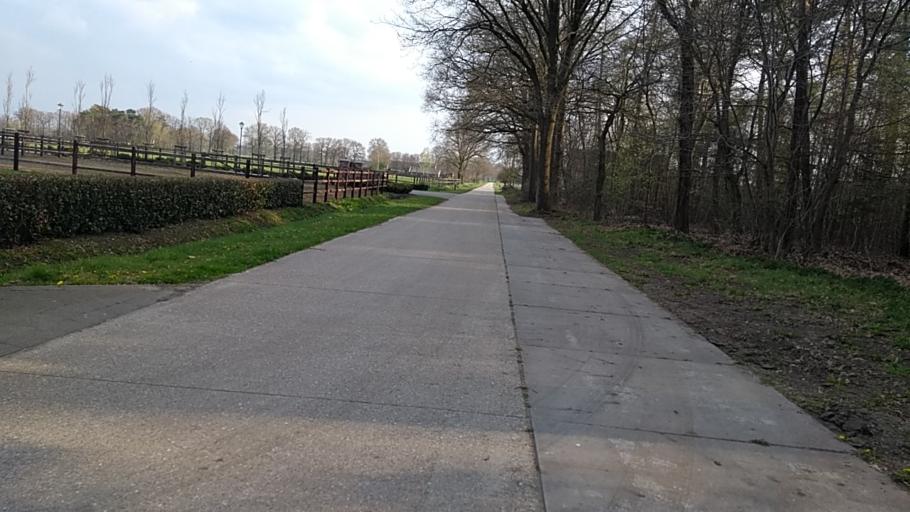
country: NL
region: Overijssel
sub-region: Gemeente Borne
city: Borne
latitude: 52.3510
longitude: 6.7272
